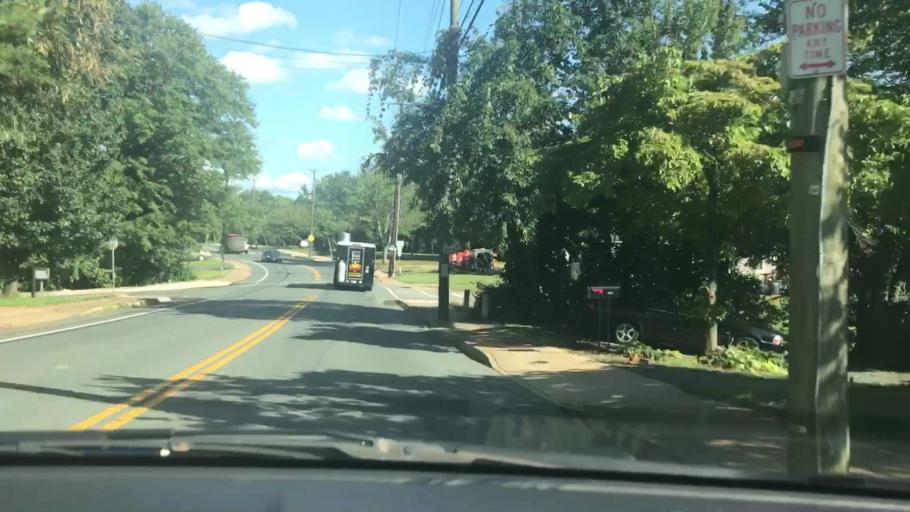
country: US
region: Virginia
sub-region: City of Charlottesville
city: Charlottesville
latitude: 38.0156
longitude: -78.5049
